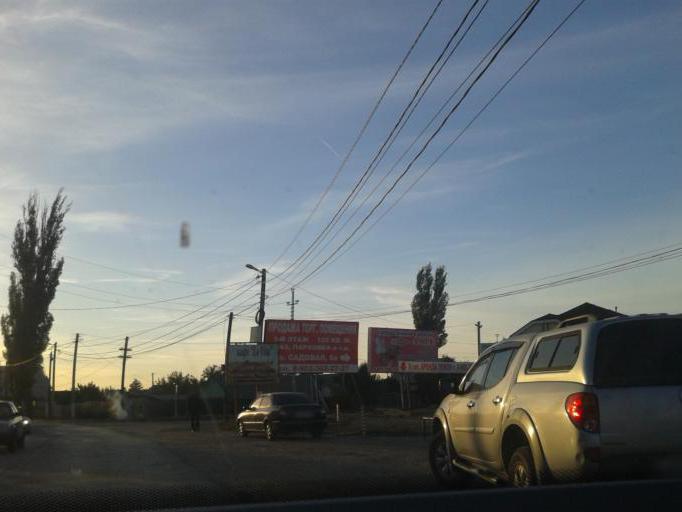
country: RU
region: Volgograd
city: Krasnoslobodsk
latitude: 48.7076
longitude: 44.5885
